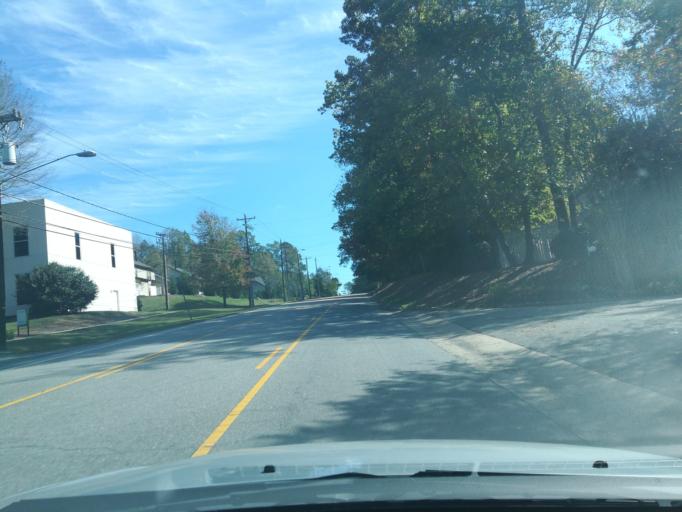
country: US
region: North Carolina
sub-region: Durham County
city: Durham
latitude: 35.9754
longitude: -78.9643
